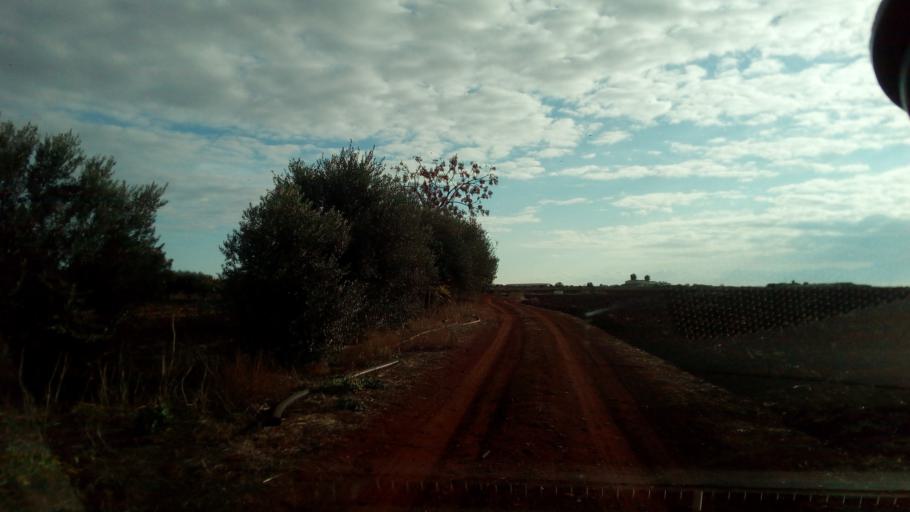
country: CY
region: Ammochostos
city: Avgorou
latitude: 35.0378
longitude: 33.8732
